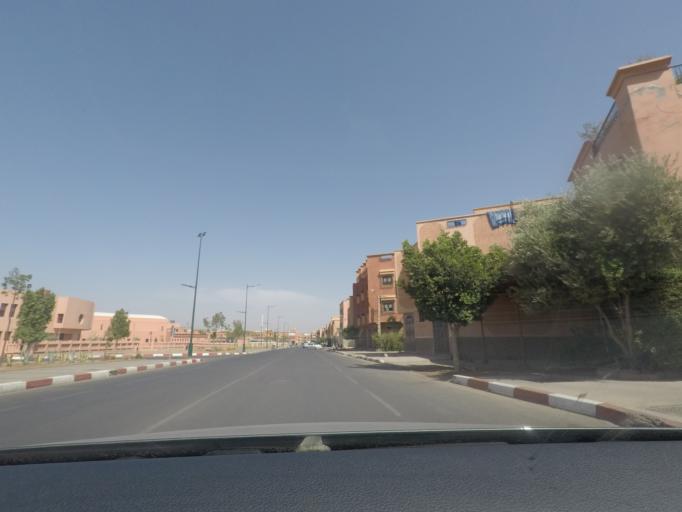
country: MA
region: Marrakech-Tensift-Al Haouz
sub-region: Marrakech
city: Marrakesh
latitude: 31.5919
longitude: -8.0273
